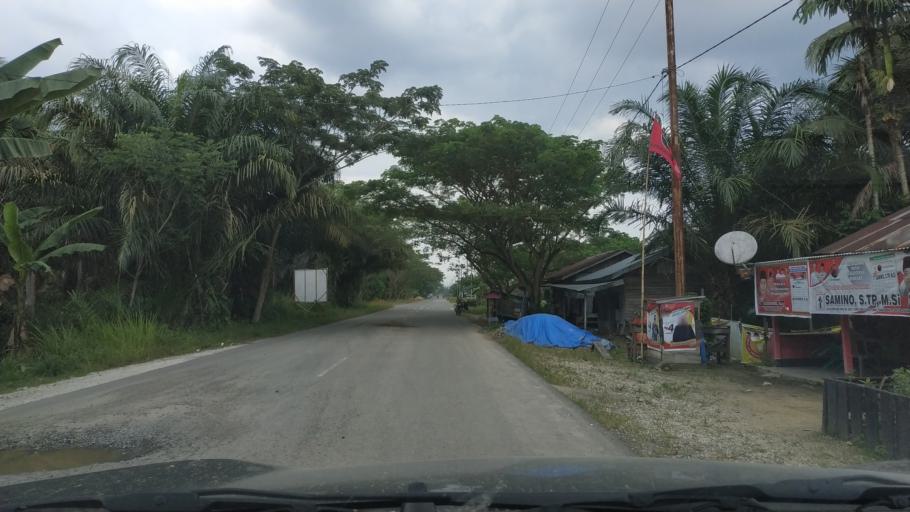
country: ID
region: Riau
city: Sungaisalak
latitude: -0.5667
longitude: 102.9709
